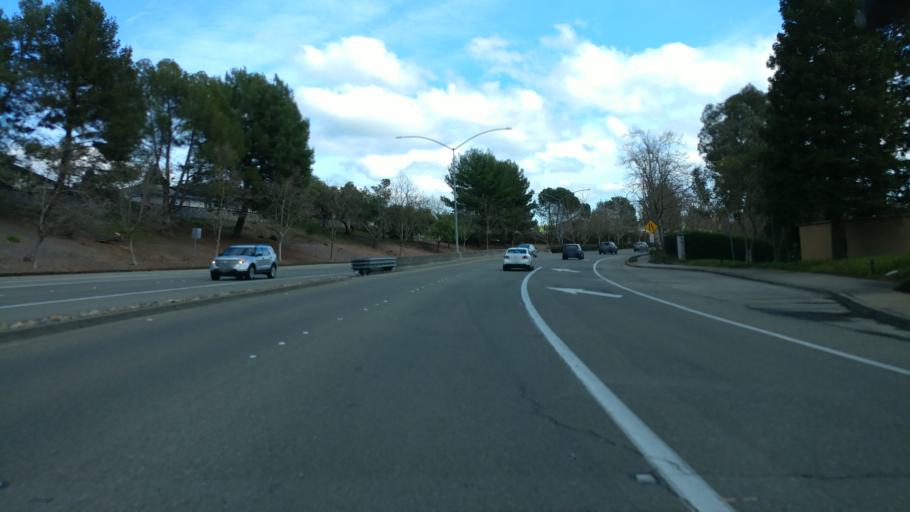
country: US
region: California
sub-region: Contra Costa County
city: San Ramon
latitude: 37.7880
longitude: -121.9463
